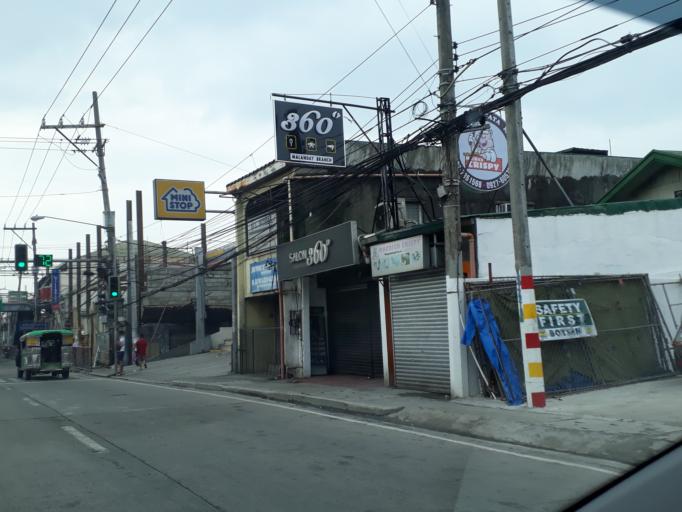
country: PH
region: Calabarzon
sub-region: Province of Rizal
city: Valenzuela
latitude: 14.7096
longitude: 120.9597
